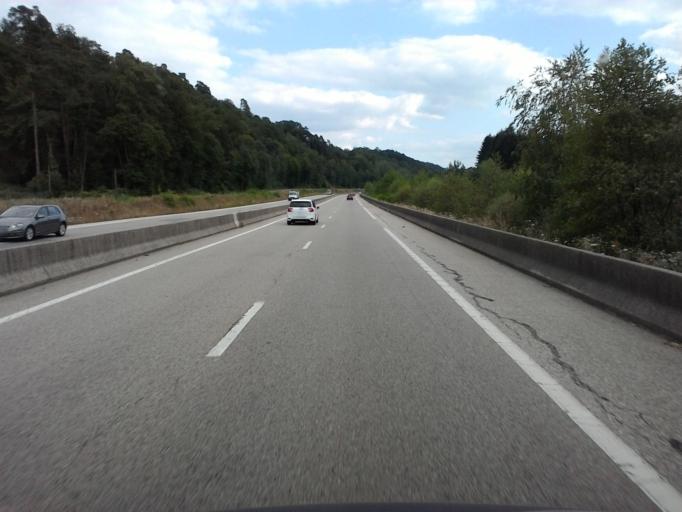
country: FR
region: Lorraine
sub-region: Departement des Vosges
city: Arches
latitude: 48.1411
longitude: 6.5121
